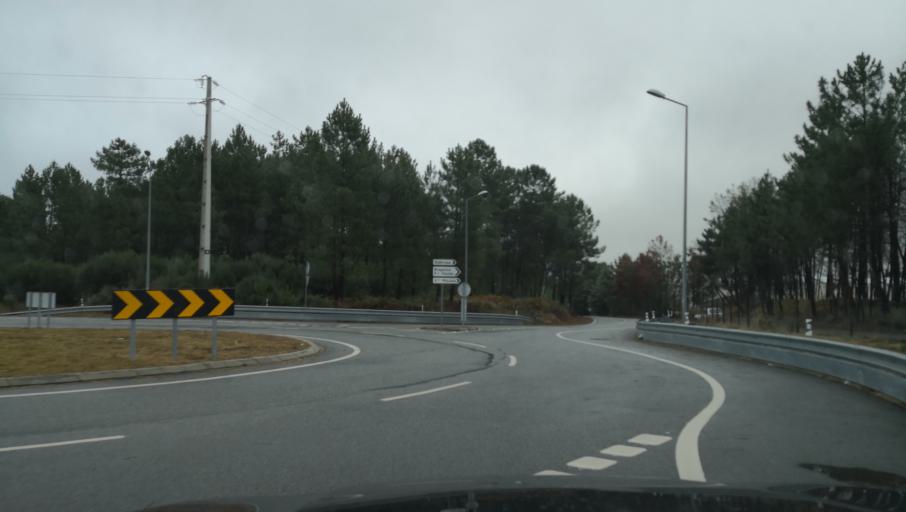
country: PT
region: Vila Real
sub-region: Sabrosa
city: Sabrosa
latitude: 41.3497
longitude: -7.5988
